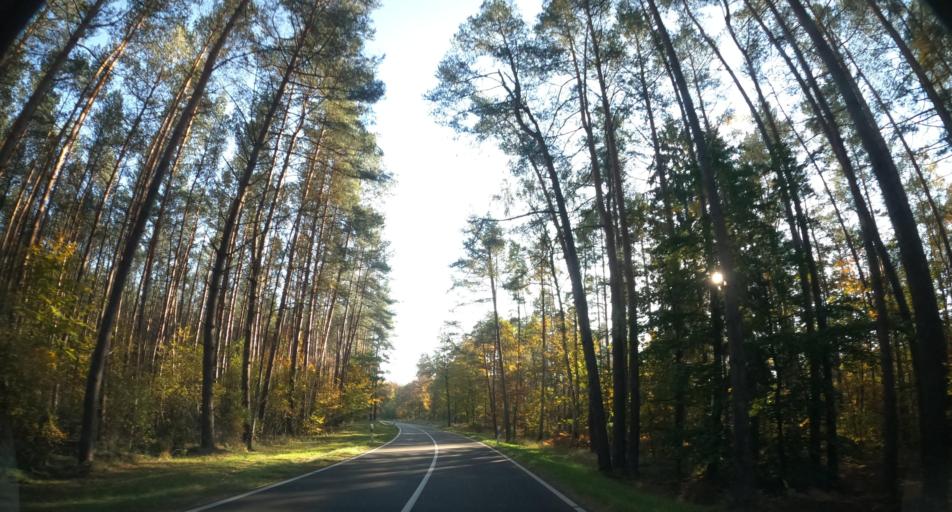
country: DE
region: Mecklenburg-Vorpommern
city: Ahlbeck
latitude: 53.6610
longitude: 14.1822
